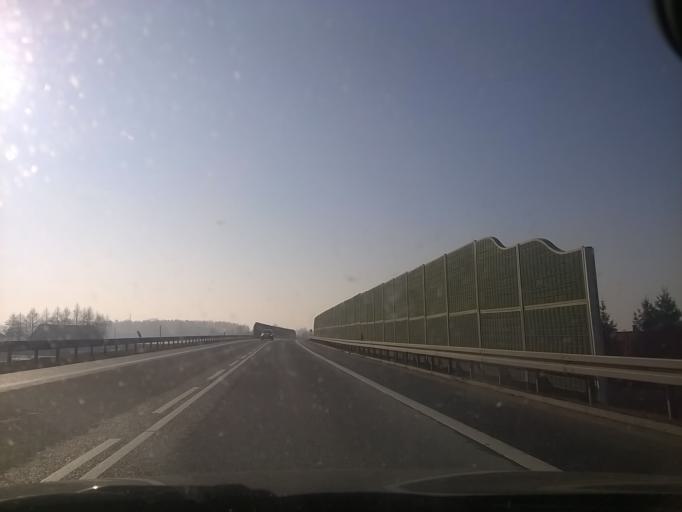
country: PL
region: Warmian-Masurian Voivodeship
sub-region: Powiat olsztynski
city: Biskupiec
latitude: 53.8372
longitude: 20.9288
